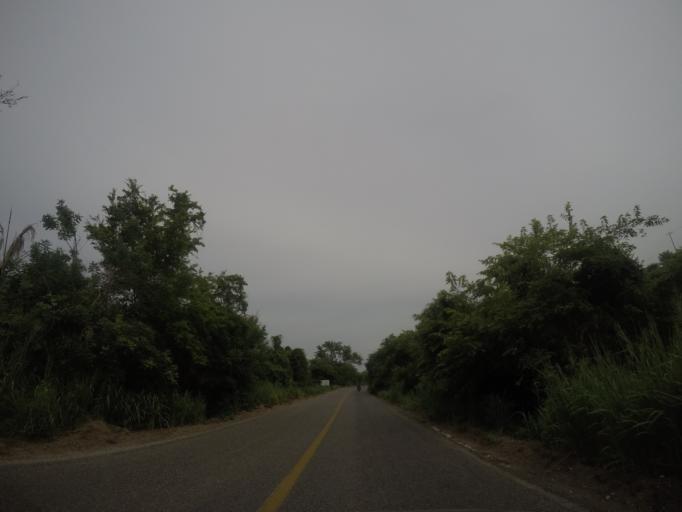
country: MX
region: Oaxaca
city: San Pedro Mixtepec
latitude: 15.9282
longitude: -97.1513
